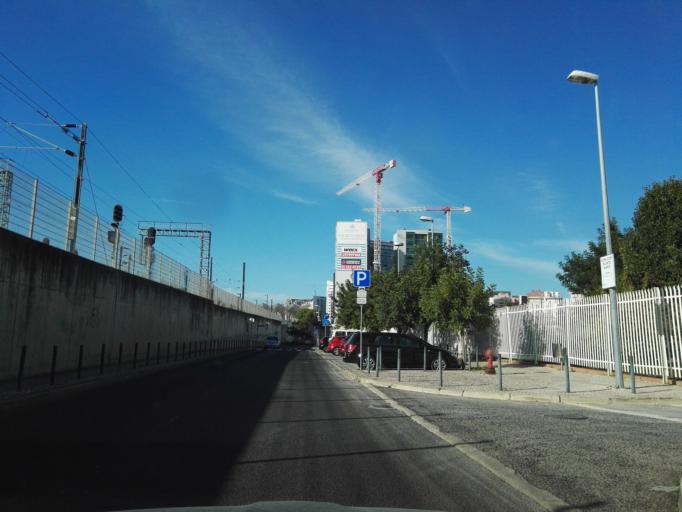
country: PT
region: Lisbon
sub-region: Loures
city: Moscavide
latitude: 38.7611
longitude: -9.0997
